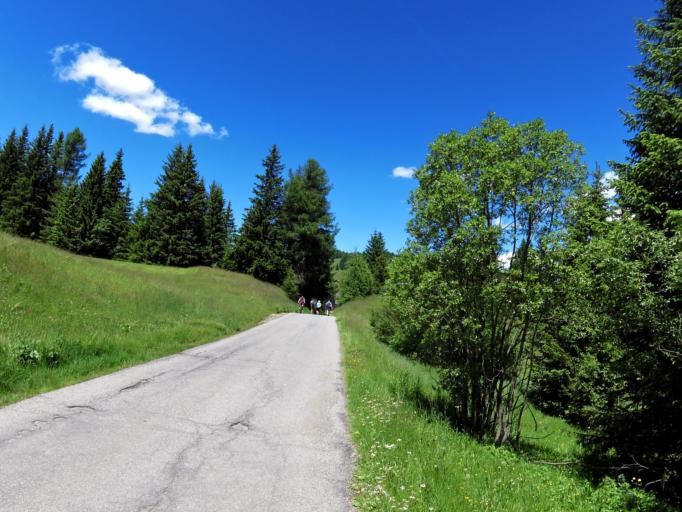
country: IT
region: Trentino-Alto Adige
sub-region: Bolzano
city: Ortisei
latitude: 46.5307
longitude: 11.6682
